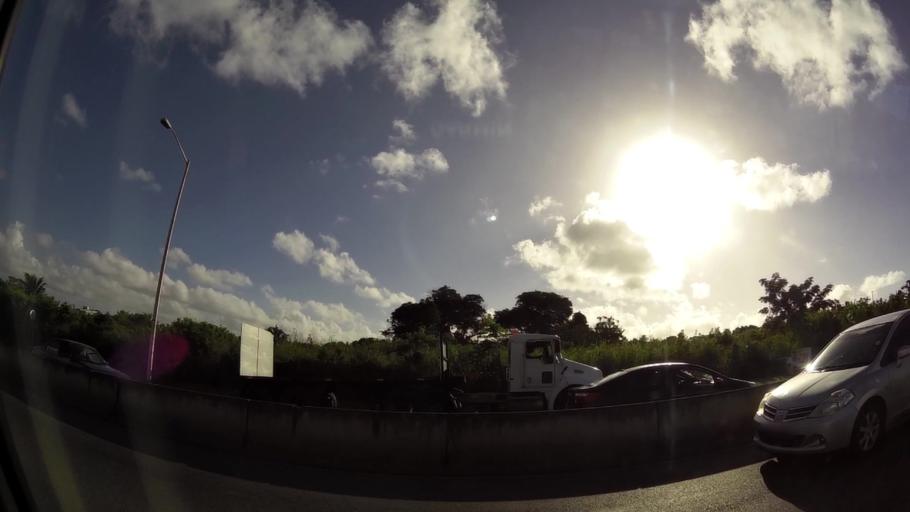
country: BB
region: Saint Michael
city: Bridgetown
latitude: 13.1038
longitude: -59.5802
